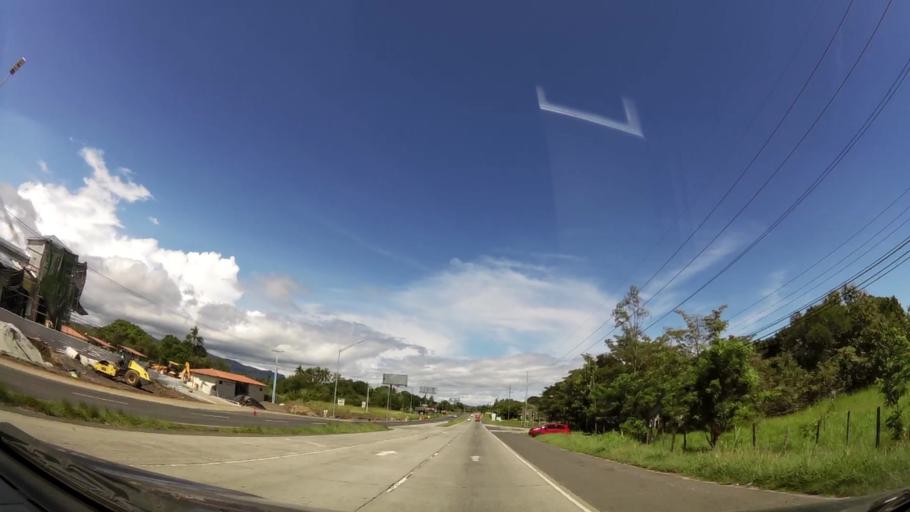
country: PA
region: Panama
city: Chame
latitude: 8.5528
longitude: -79.9076
